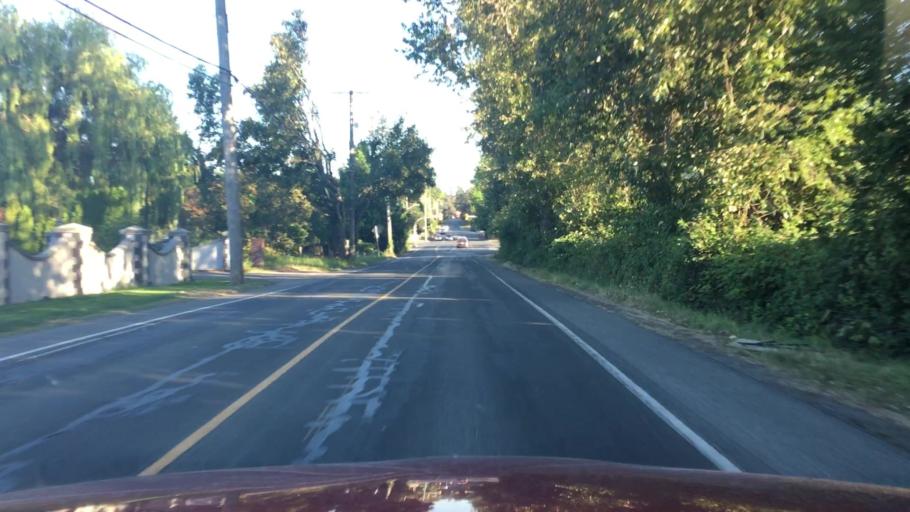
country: CA
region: British Columbia
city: Victoria
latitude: 48.4738
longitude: -123.3517
